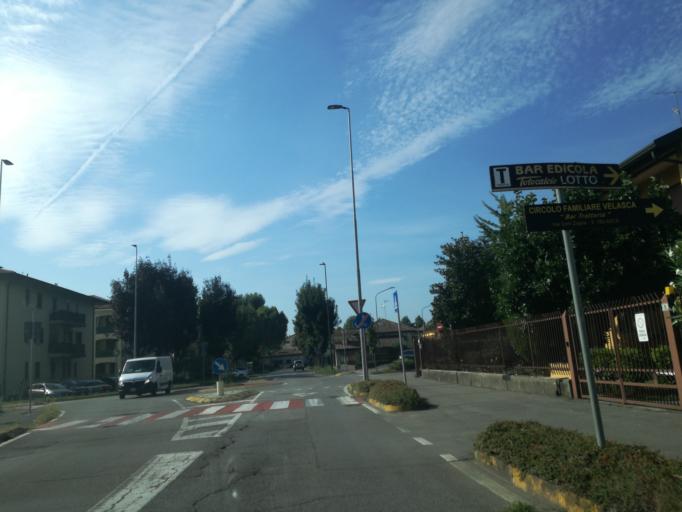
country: IT
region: Lombardy
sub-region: Provincia di Monza e Brianza
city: Velasca
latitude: 45.6337
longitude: 9.3529
